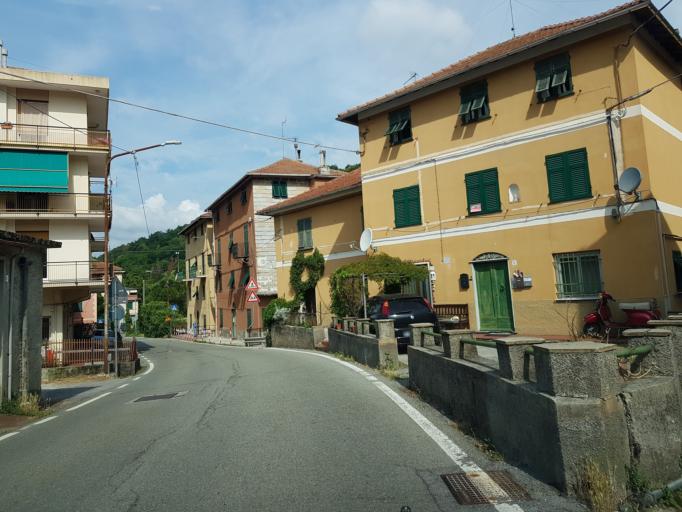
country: IT
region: Liguria
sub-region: Provincia di Genova
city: Piccarello
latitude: 44.4835
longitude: 8.9625
